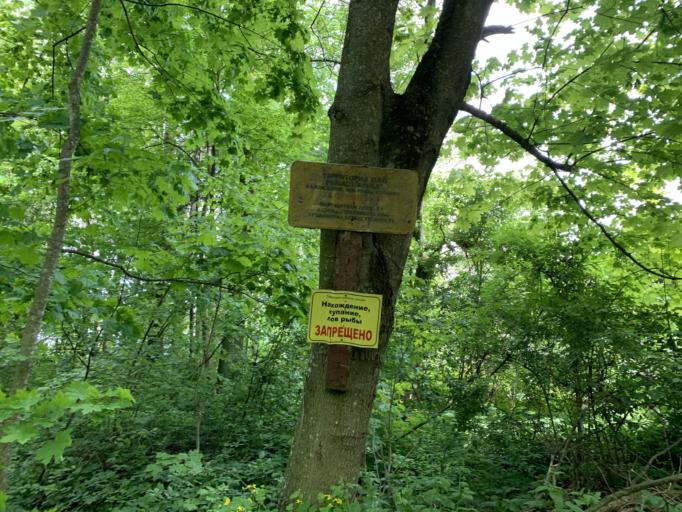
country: BY
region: Minsk
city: Nyasvizh
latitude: 53.1980
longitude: 26.6563
